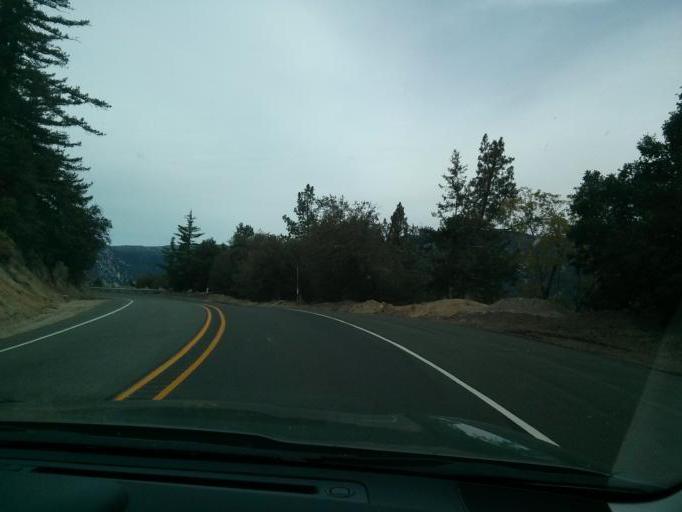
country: US
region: California
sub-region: San Bernardino County
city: Big Bear Lake
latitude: 34.1523
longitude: -116.9706
